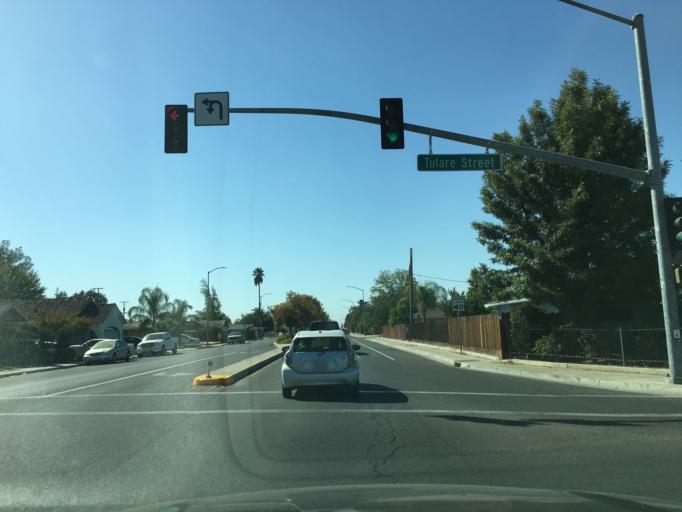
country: US
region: California
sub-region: Madera County
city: Madera
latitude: 36.9746
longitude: -120.0514
